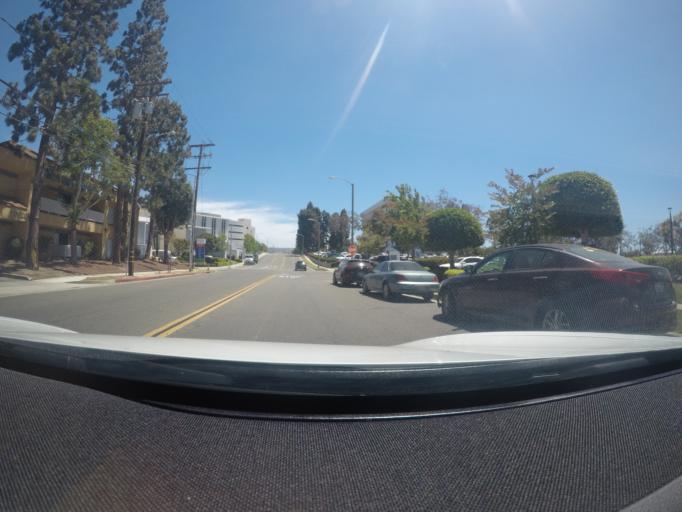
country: US
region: California
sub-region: Los Angeles County
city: Torrance
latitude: 33.8400
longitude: -118.3581
